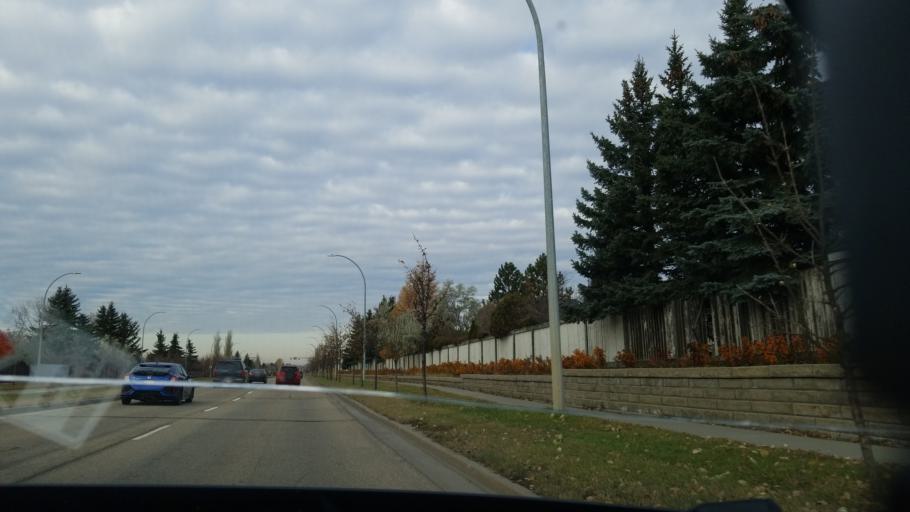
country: CA
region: Alberta
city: Edmonton
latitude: 53.6160
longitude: -113.4453
